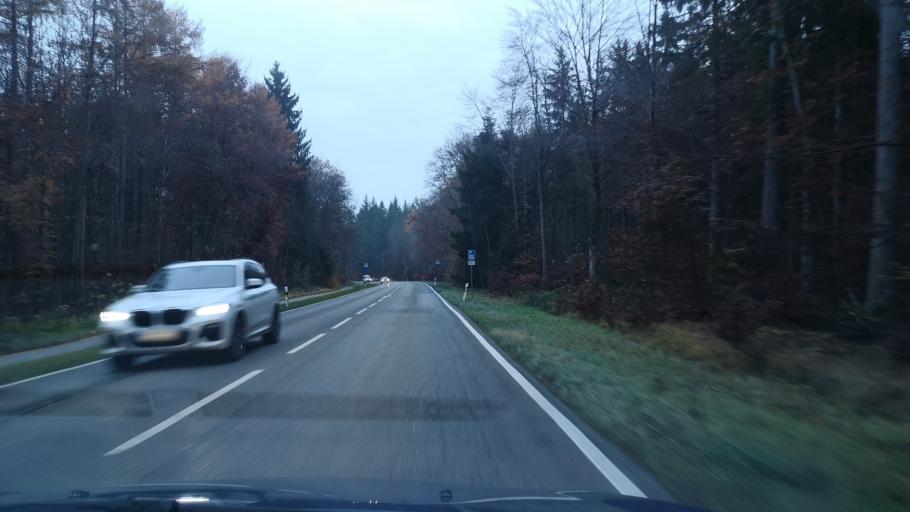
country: DE
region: Bavaria
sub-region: Upper Bavaria
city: Ebersberg
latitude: 48.1119
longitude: 11.9543
